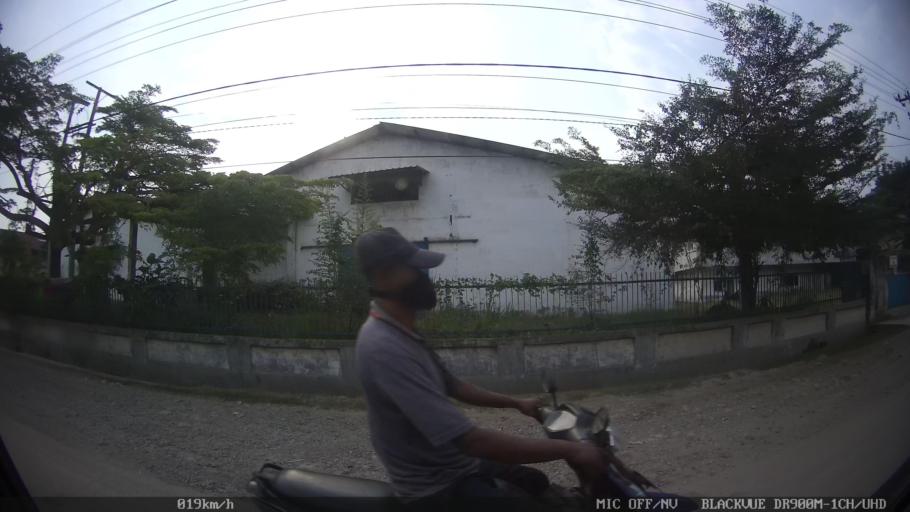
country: ID
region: Lampung
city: Panjang
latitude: -5.4478
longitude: 105.3099
